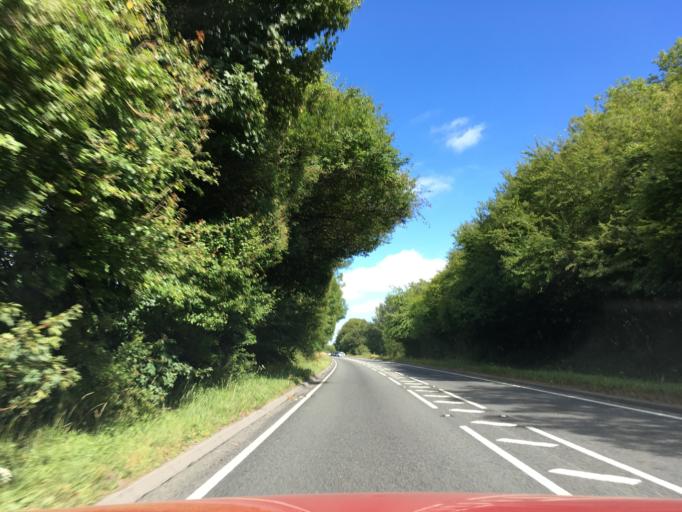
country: GB
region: England
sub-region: Dorset
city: Dorchester
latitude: 50.7437
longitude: -2.5049
